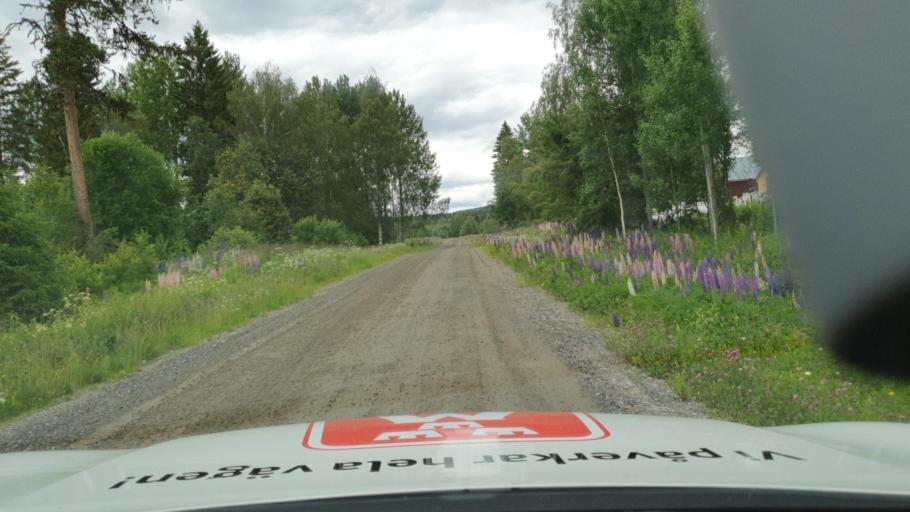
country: SE
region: Vaesterbotten
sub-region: Bjurholms Kommun
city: Bjurholm
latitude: 63.7970
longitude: 19.0869
